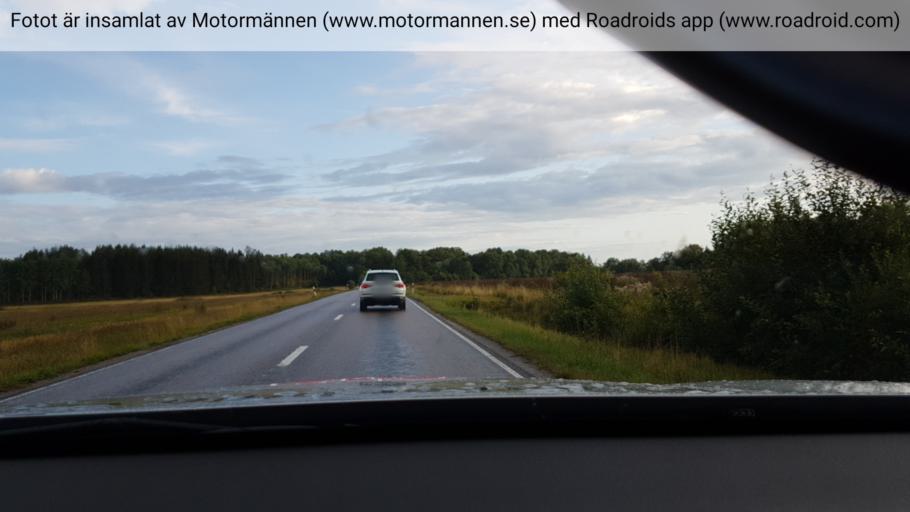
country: SE
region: Stockholm
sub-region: Norrtalje Kommun
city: Norrtalje
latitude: 59.8250
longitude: 18.6544
